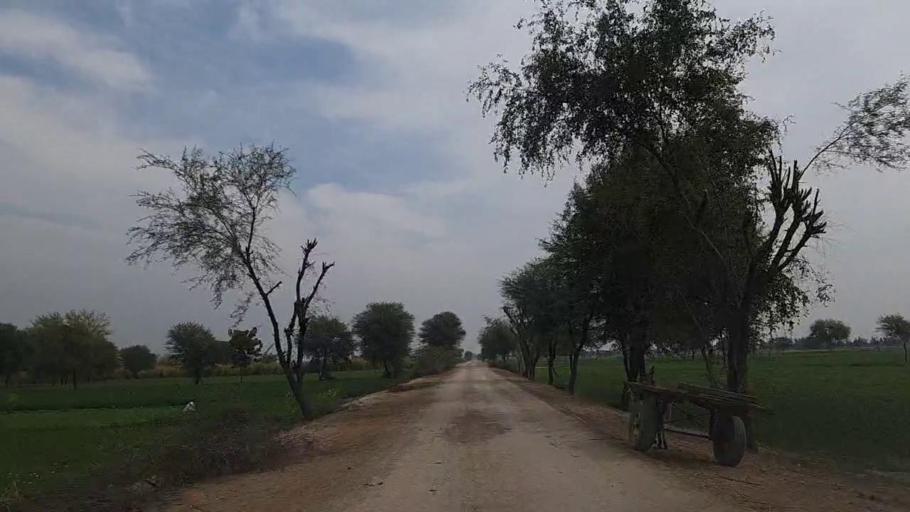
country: PK
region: Sindh
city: Daur
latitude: 26.4451
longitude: 68.4592
